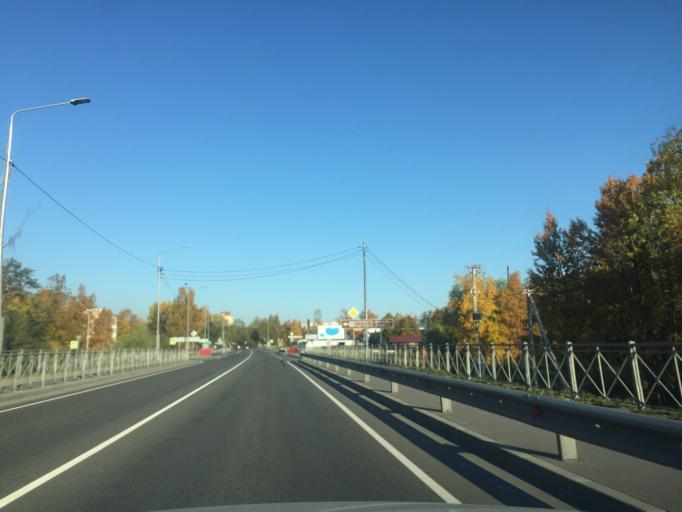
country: RU
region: Leningrad
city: Priozersk
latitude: 61.0308
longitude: 30.1257
